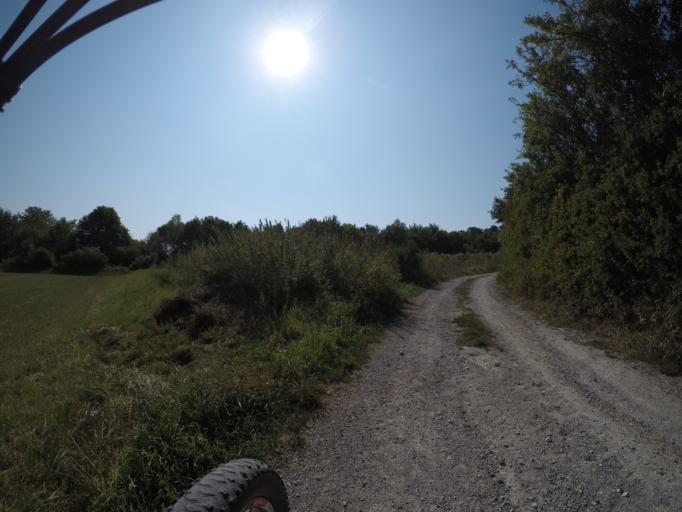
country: AT
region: Lower Austria
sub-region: Politischer Bezirk Baden
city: Hirtenberg
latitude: 47.9481
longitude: 16.1698
